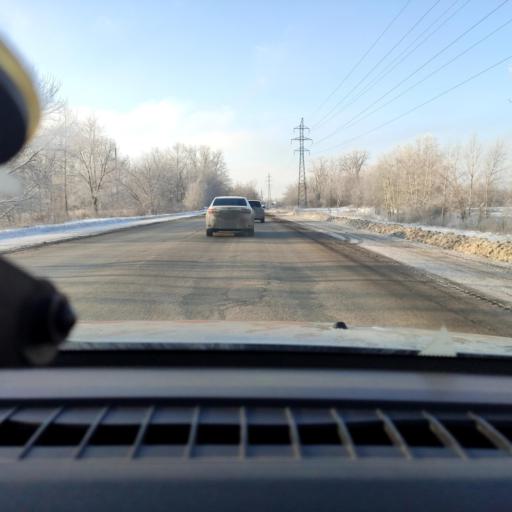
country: RU
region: Samara
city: Rozhdestveno
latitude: 53.1379
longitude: 50.0579
